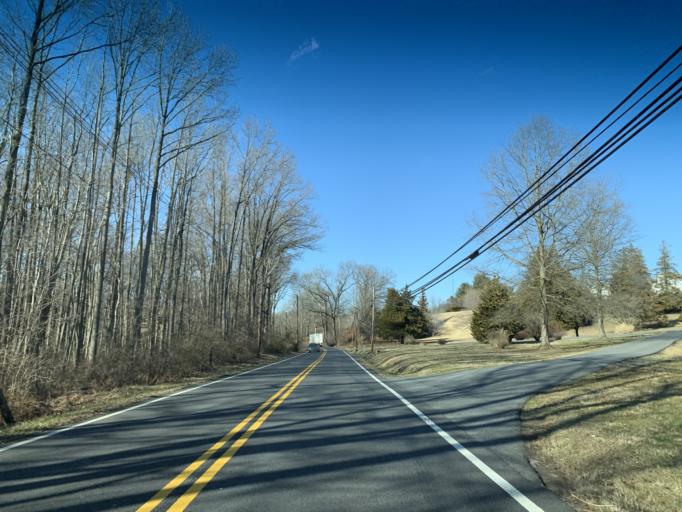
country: US
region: Maryland
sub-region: Cecil County
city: Elkton
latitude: 39.6379
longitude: -75.8643
